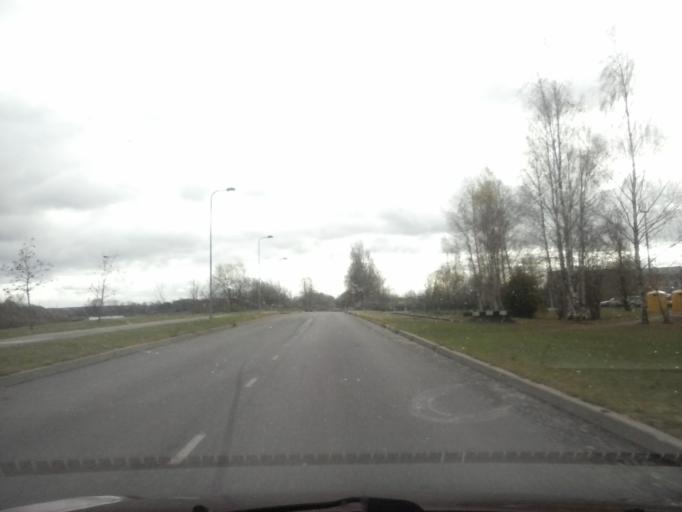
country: EE
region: Tartu
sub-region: Tartu linn
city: Tartu
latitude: 58.3659
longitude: 26.7471
